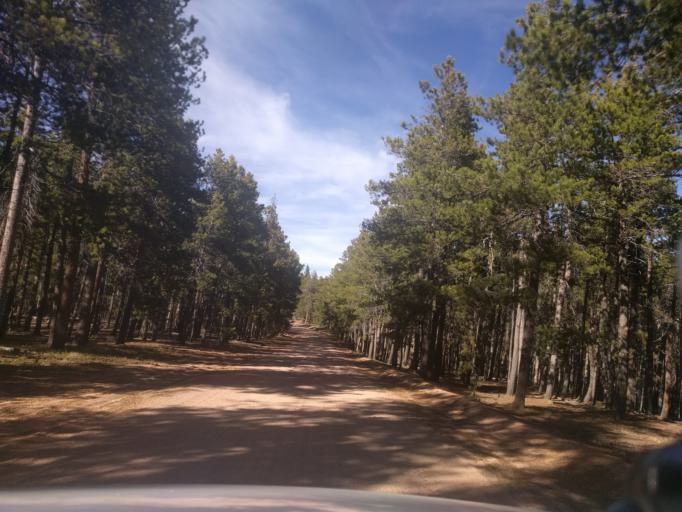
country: US
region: Colorado
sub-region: Douglas County
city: Perry Park
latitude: 39.2123
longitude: -105.0570
